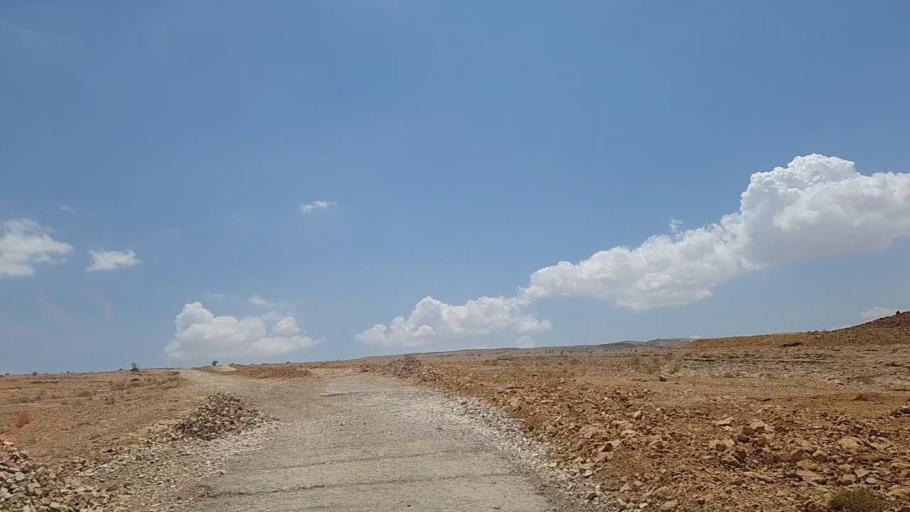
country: PK
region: Sindh
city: Bhan
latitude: 26.2878
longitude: 67.5785
